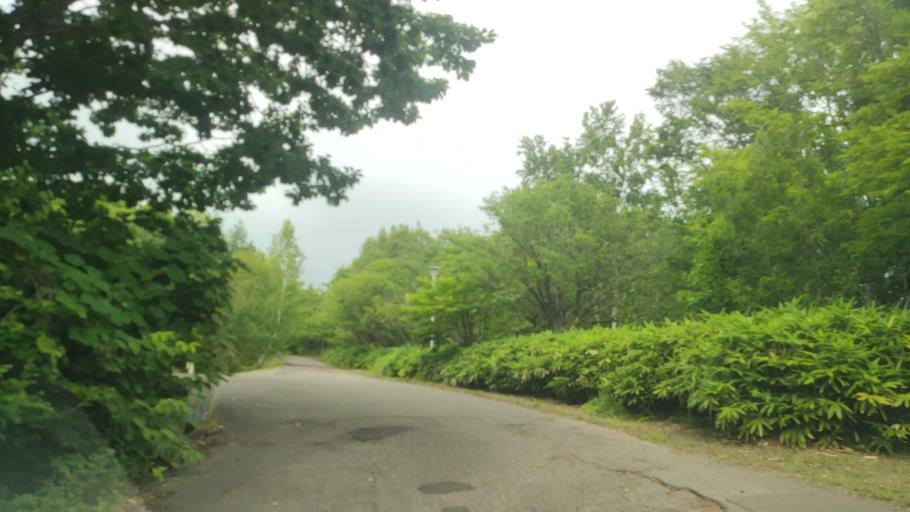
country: JP
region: Hokkaido
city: Otaru
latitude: 43.1970
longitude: 140.9830
